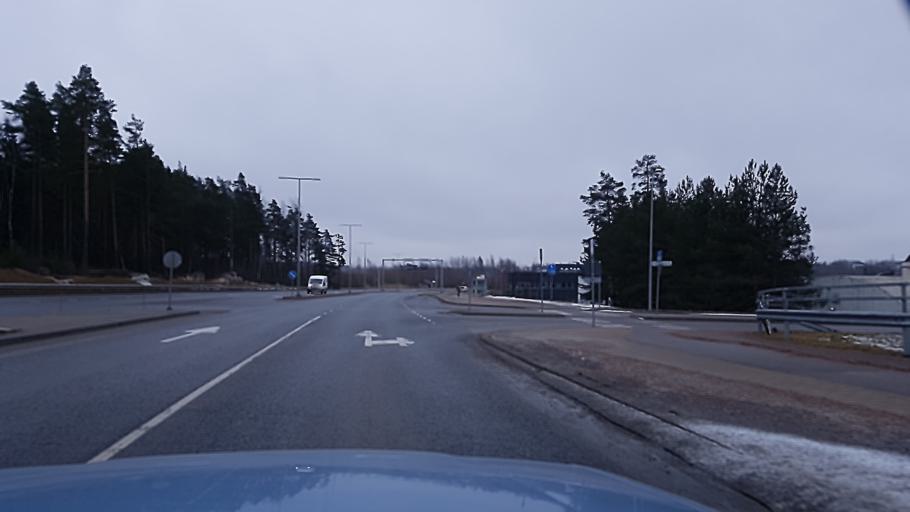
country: FI
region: Uusimaa
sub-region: Helsinki
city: Vantaa
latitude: 60.3008
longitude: 24.9648
